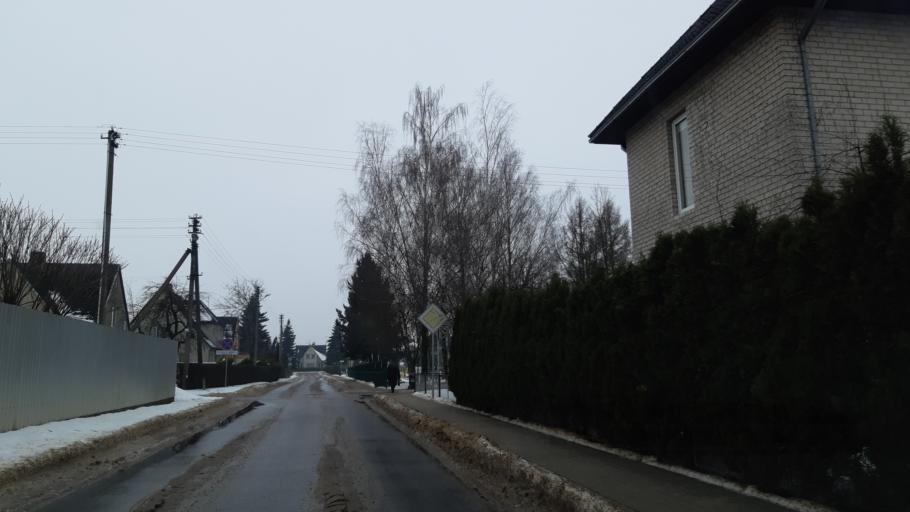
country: LT
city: Vilkaviskis
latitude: 54.6458
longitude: 23.0348
